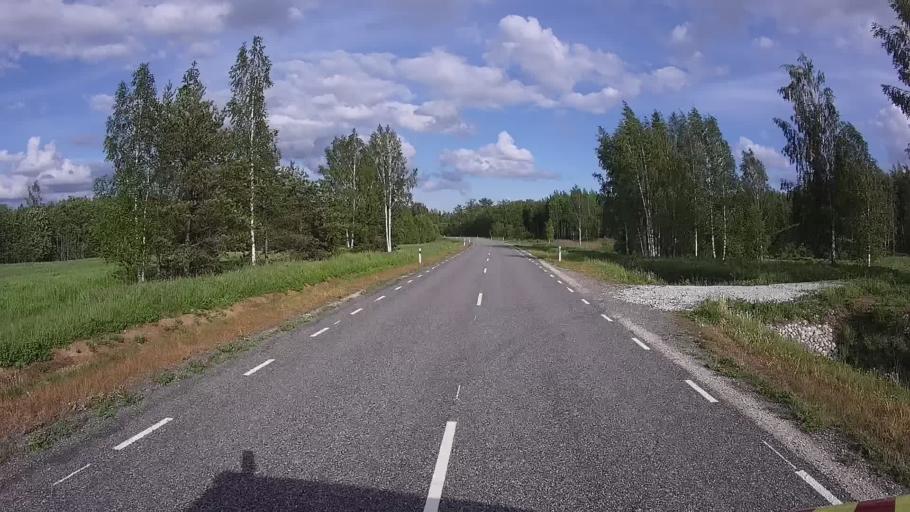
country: EE
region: Jogevamaa
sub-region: Mustvee linn
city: Mustvee
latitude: 59.0239
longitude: 27.0384
